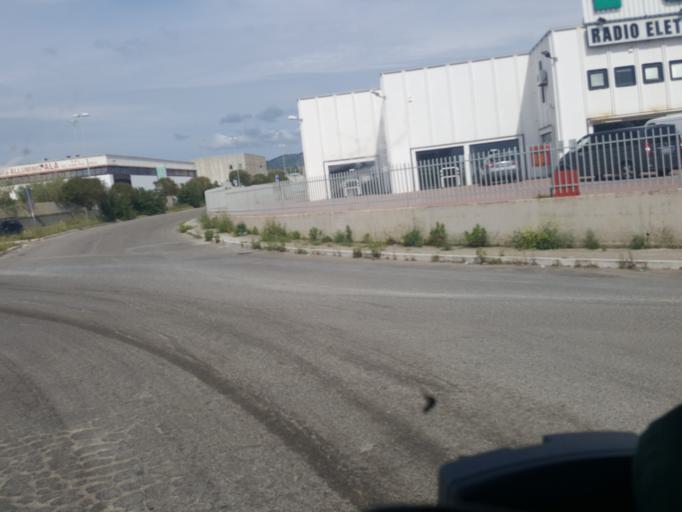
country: IT
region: Latium
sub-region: Citta metropolitana di Roma Capitale
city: Aurelia
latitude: 42.1199
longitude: 11.7785
